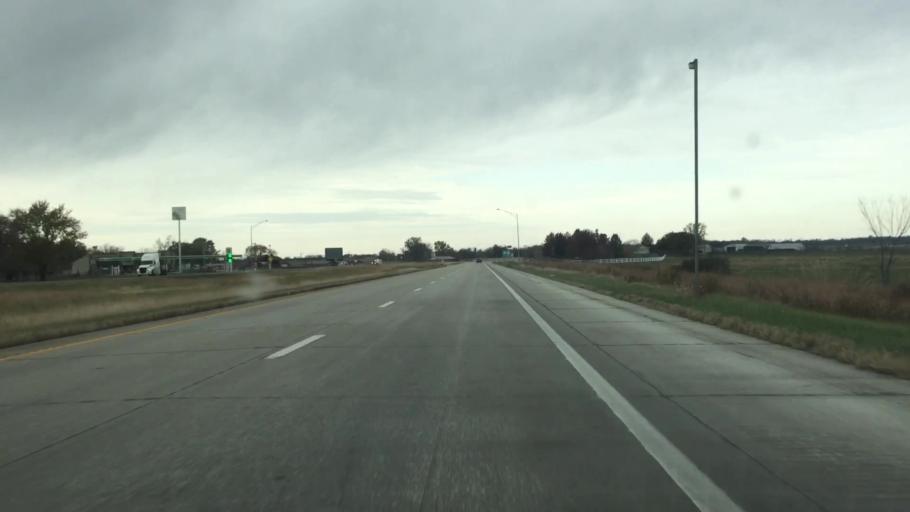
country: US
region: Missouri
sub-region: Saint Clair County
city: Osceola
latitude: 38.1407
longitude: -93.7184
